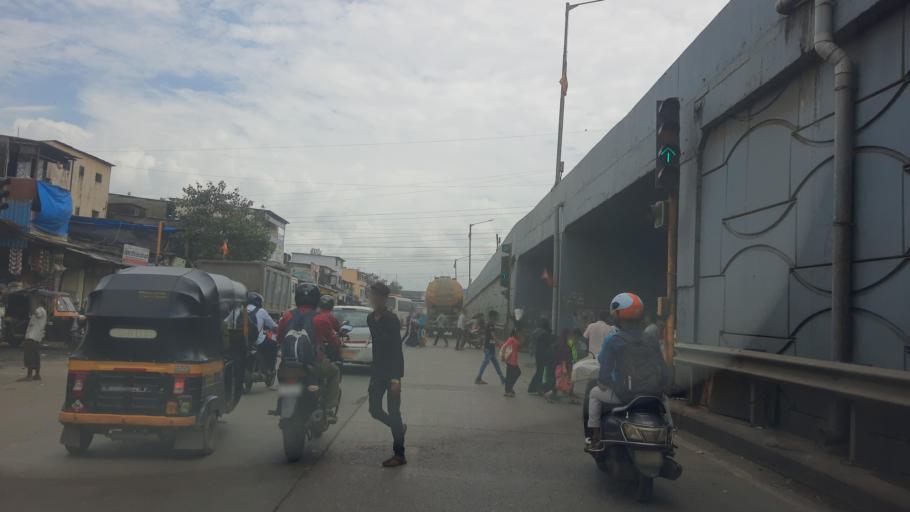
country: IN
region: Maharashtra
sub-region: Mumbai Suburban
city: Mumbai
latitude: 19.0534
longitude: 72.9355
